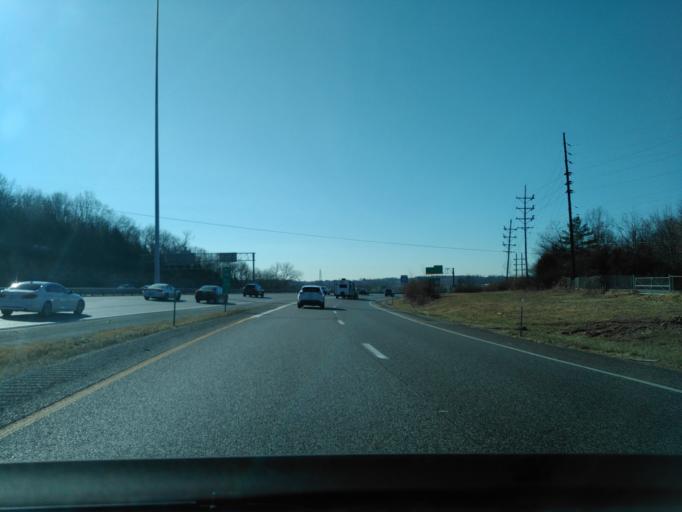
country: US
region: Missouri
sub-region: Saint Louis County
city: Sunset Hills
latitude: 38.5454
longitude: -90.4309
